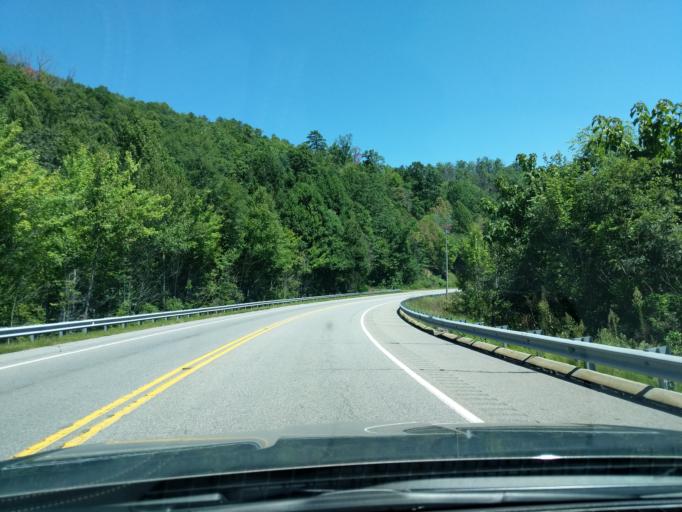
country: US
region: North Carolina
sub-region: Macon County
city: Franklin
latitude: 35.1350
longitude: -83.5134
